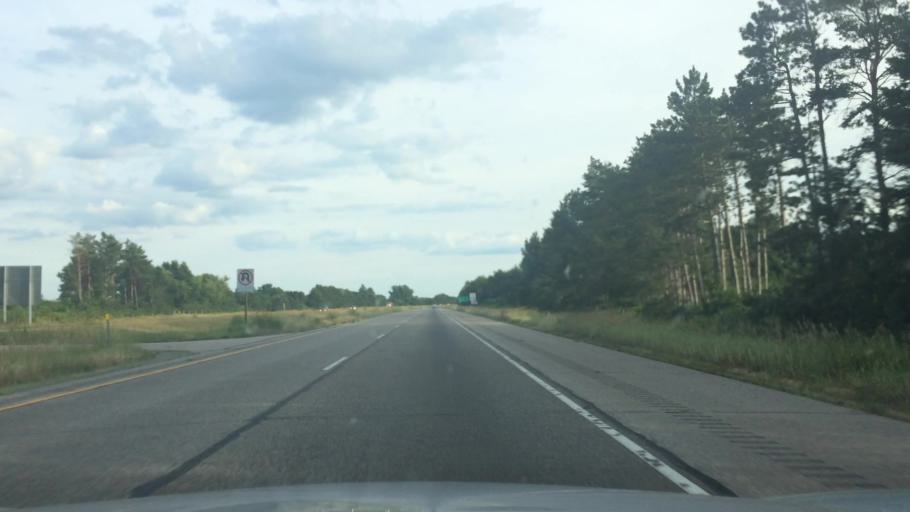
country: US
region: Wisconsin
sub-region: Portage County
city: Plover
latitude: 44.2045
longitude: -89.5236
